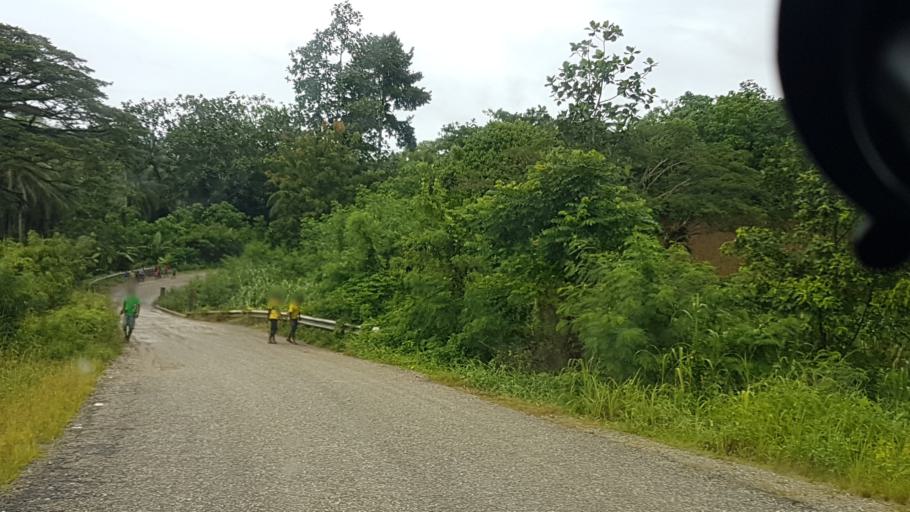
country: PG
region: East Sepik
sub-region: Wewak
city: Wewak
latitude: -3.6892
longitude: 143.1089
